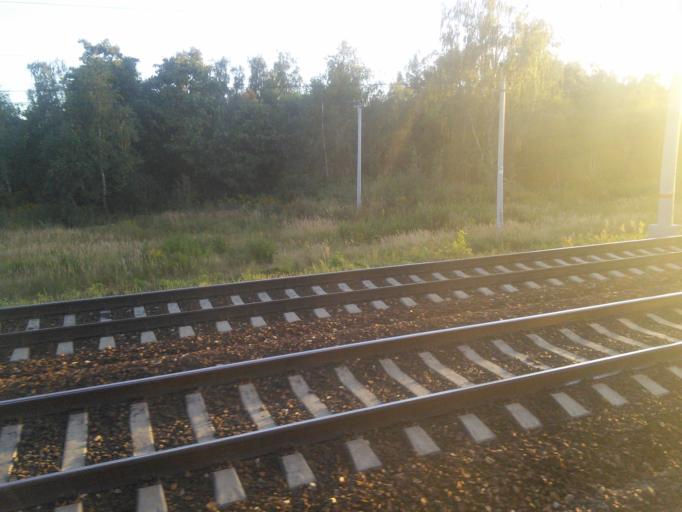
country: RU
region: Moskovskaya
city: Kupavna
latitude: 55.7484
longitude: 38.1389
